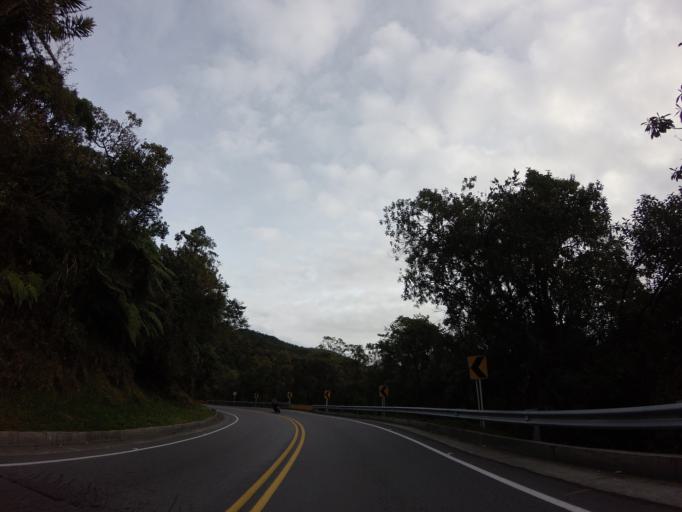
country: CO
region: Tolima
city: Herveo
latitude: 5.0991
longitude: -75.2774
